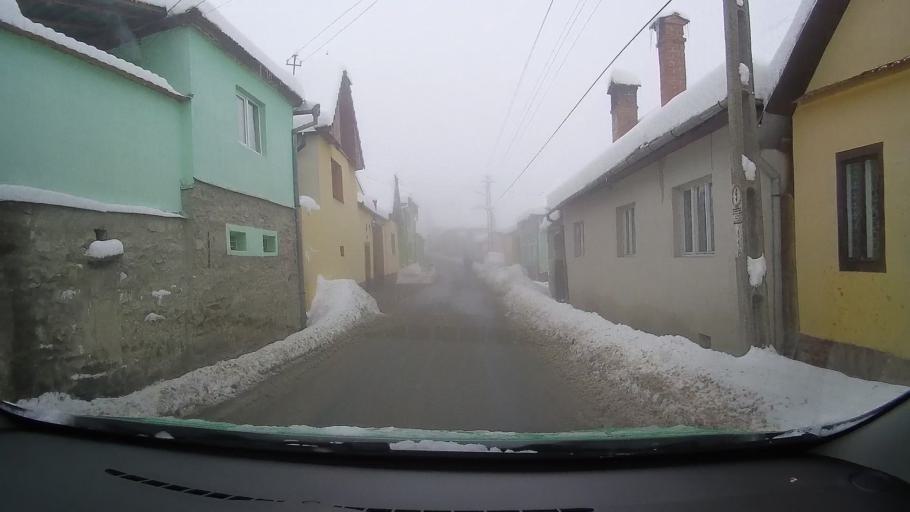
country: RO
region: Sibiu
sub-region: Comuna Poiana Sibiului
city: Poiana Sibiului
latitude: 45.8014
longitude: 23.7807
